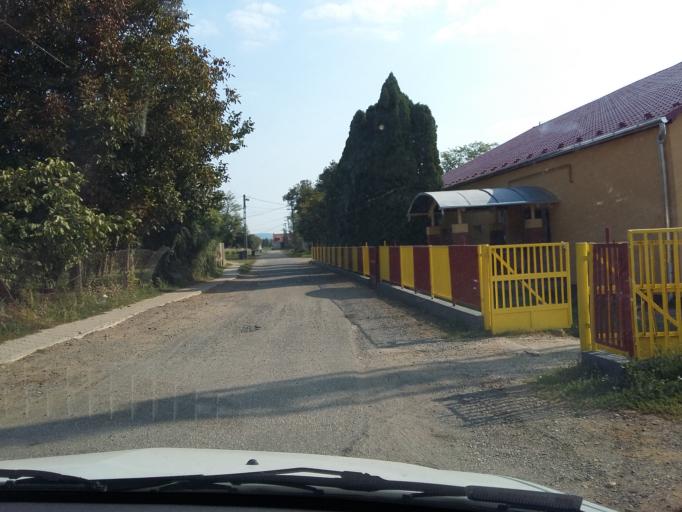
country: HU
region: Borsod-Abauj-Zemplen
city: Bekecs
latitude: 48.1521
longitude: 21.1769
